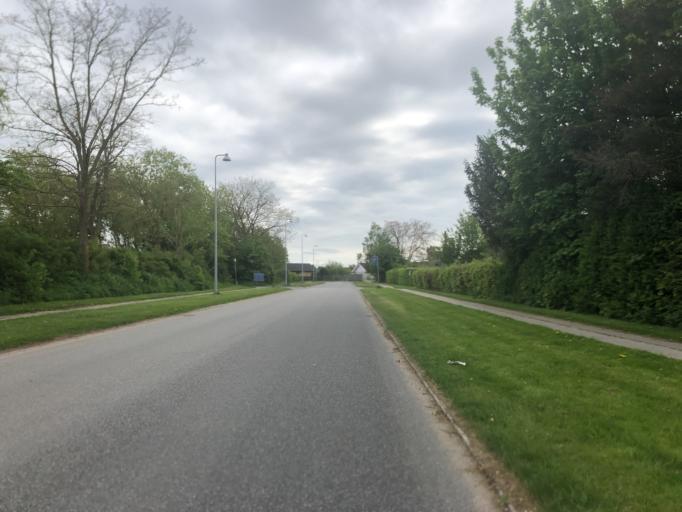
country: DK
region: Zealand
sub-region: Koge Kommune
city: Koge
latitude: 55.4442
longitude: 12.1624
